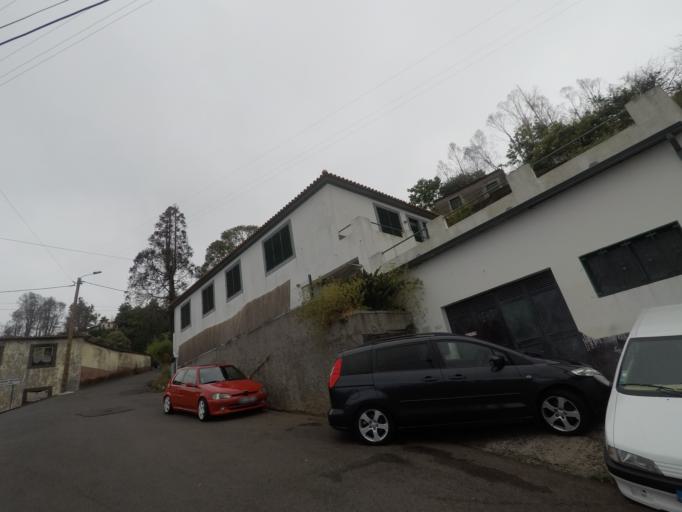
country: PT
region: Madeira
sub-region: Funchal
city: Nossa Senhora do Monte
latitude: 32.6708
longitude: -16.8862
